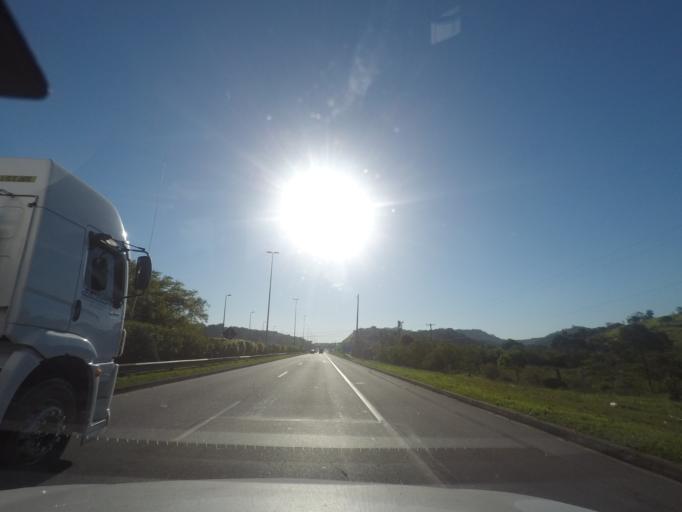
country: BR
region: Rio de Janeiro
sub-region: Petropolis
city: Petropolis
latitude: -22.6504
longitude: -43.1705
